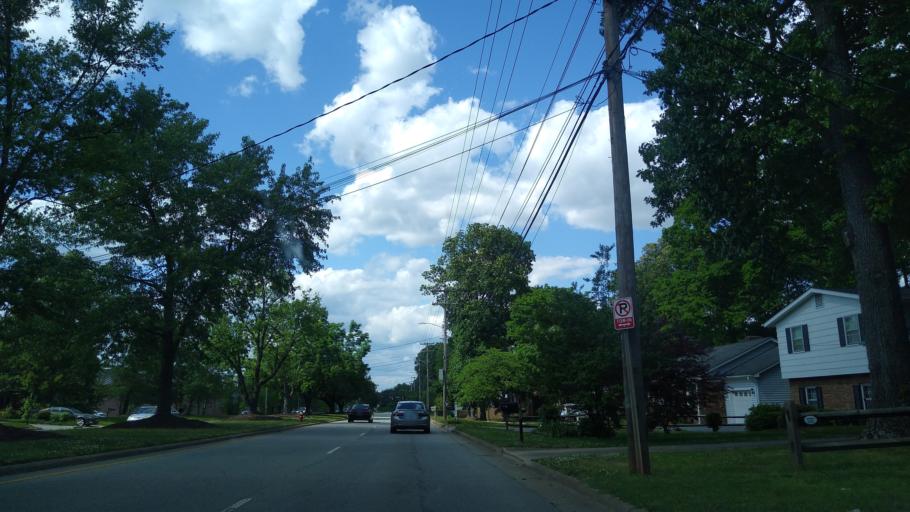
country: US
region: North Carolina
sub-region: Guilford County
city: High Point
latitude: 36.0058
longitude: -80.0099
